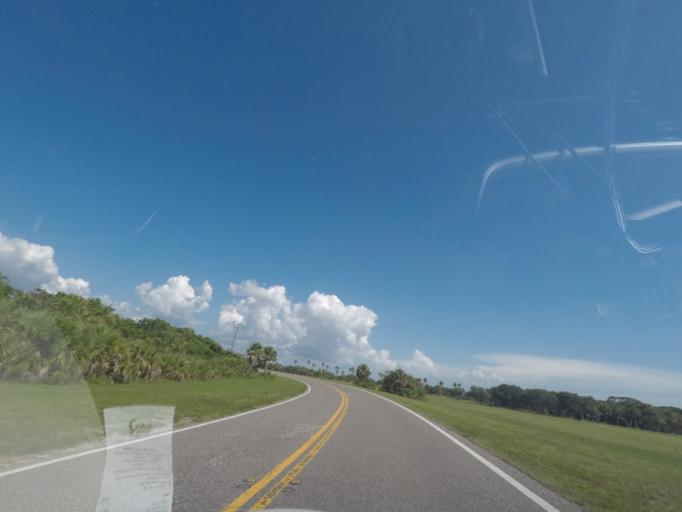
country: US
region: Florida
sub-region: Pinellas County
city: Tierra Verde
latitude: 27.6164
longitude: -82.7346
